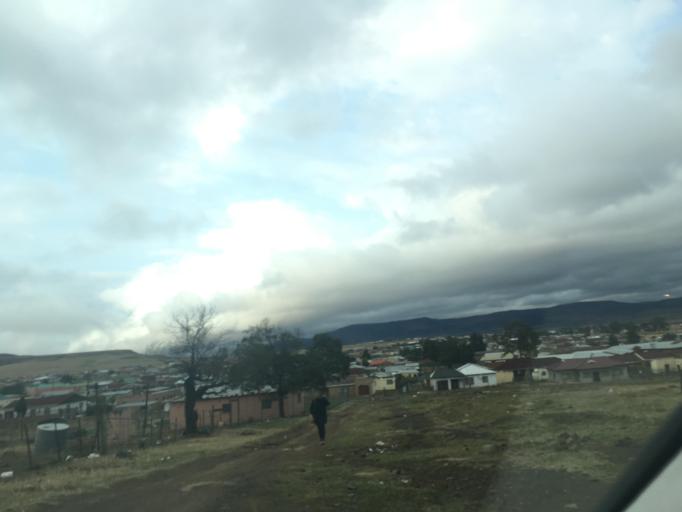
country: ZA
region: Eastern Cape
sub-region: Chris Hani District Municipality
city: Cala
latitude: -31.5283
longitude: 27.6984
